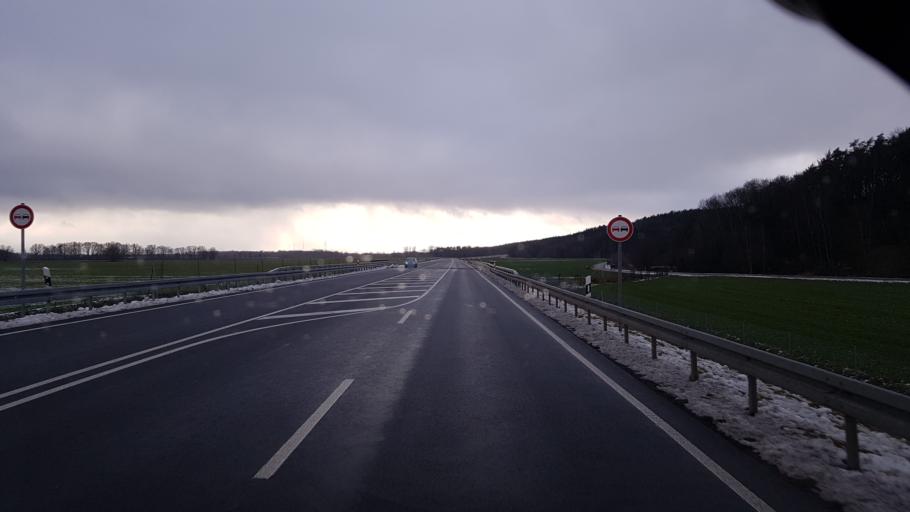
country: DE
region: Brandenburg
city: Schenkendobern
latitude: 51.8689
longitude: 14.6211
